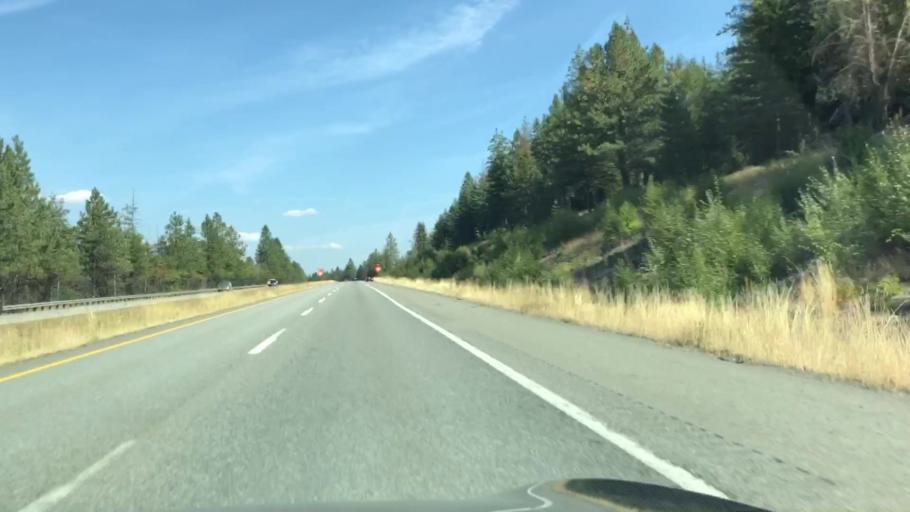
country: US
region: Idaho
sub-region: Shoshone County
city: Pinehurst
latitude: 47.5513
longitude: -116.3090
